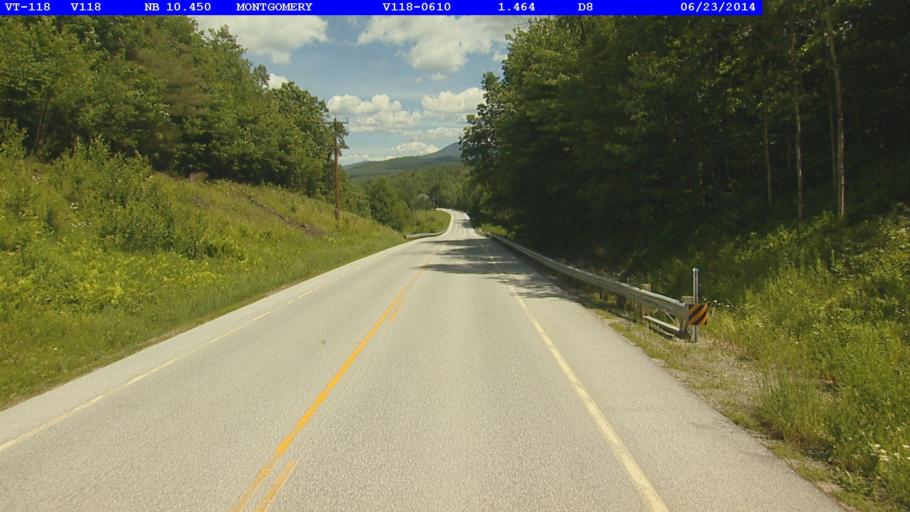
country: US
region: Vermont
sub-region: Franklin County
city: Richford
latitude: 44.8196
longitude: -72.6128
